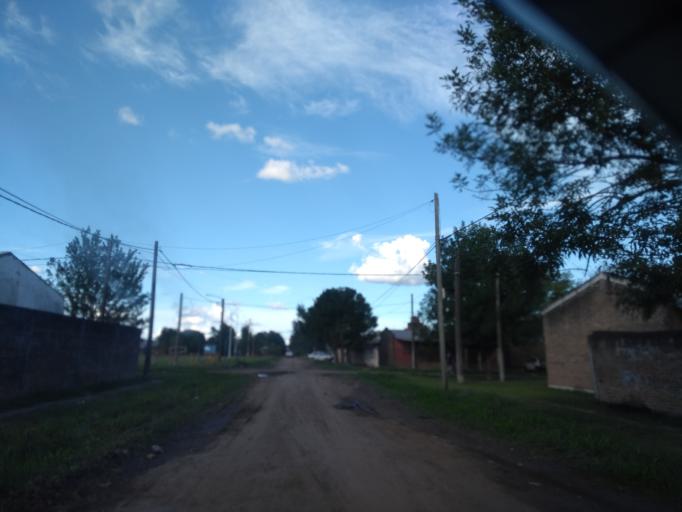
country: AR
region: Chaco
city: Fontana
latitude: -27.4138
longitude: -59.0408
